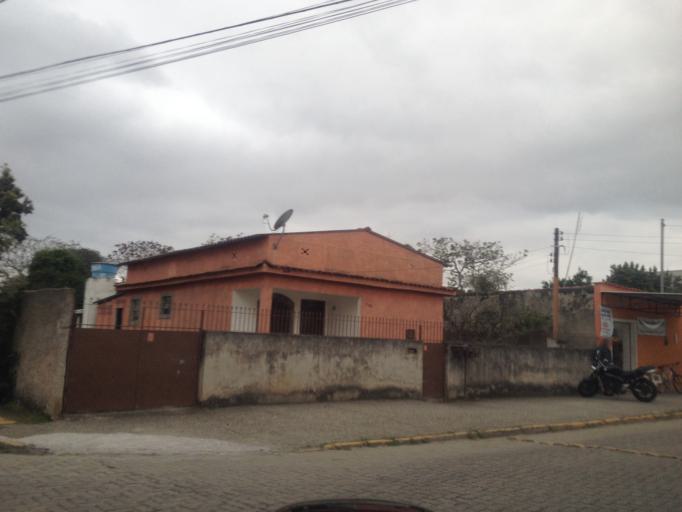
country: BR
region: Rio de Janeiro
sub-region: Porto Real
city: Porto Real
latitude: -22.4105
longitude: -44.2979
